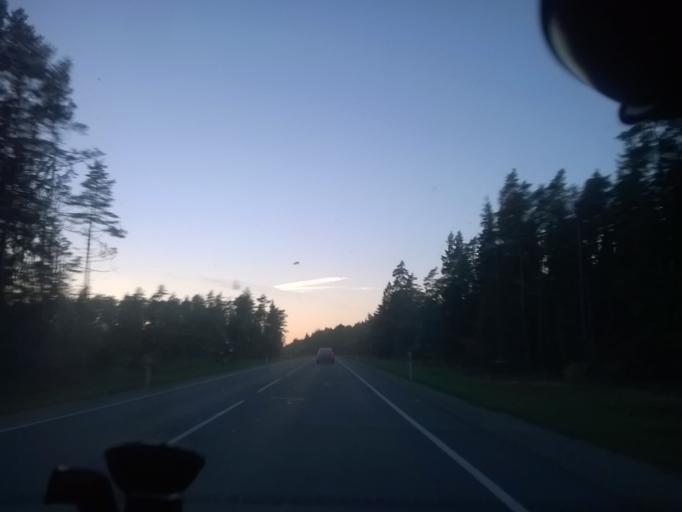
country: EE
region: Laeaene
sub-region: Lihula vald
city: Lihula
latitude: 58.9738
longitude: 23.9318
